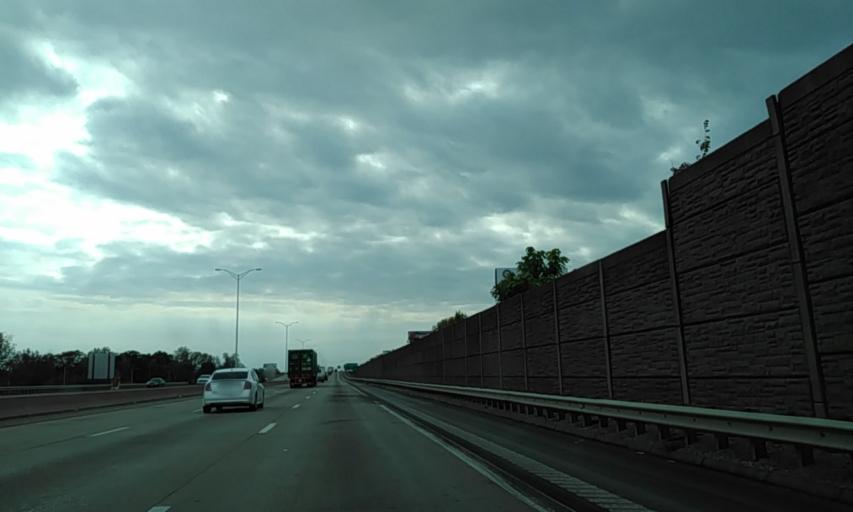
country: US
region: Illinois
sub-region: Saint Clair County
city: Centreville
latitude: 38.5751
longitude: -90.1178
